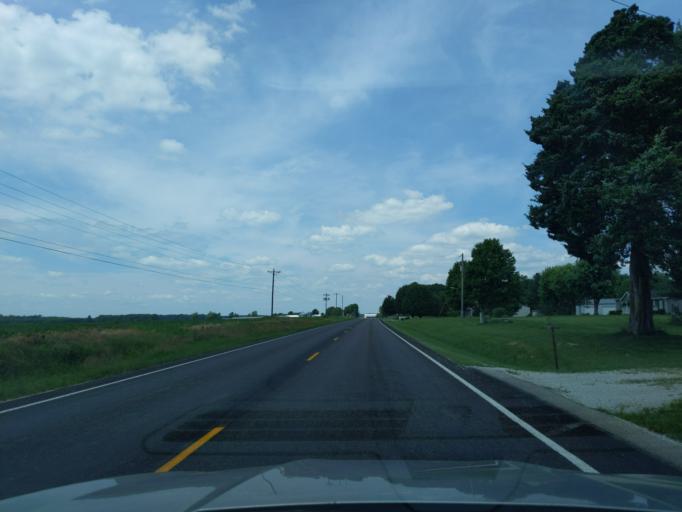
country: US
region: Indiana
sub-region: Ripley County
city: Osgood
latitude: 39.2221
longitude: -85.3352
